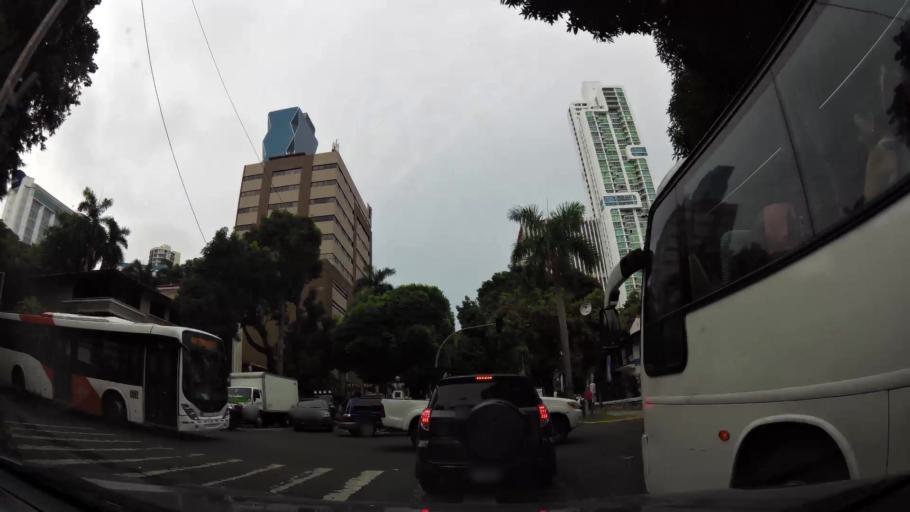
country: PA
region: Panama
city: Panama
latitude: 8.9787
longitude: -79.5273
